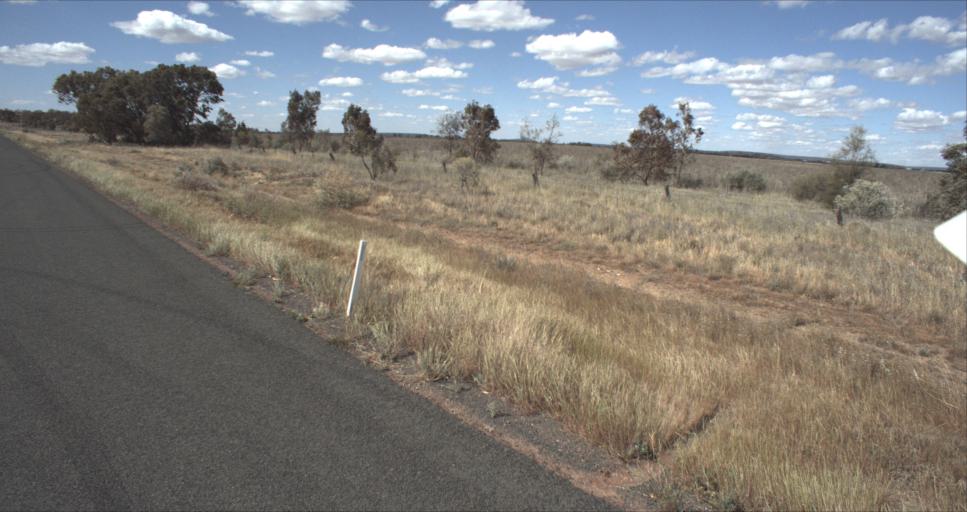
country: AU
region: New South Wales
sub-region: Leeton
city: Leeton
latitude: -34.4322
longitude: 146.2580
